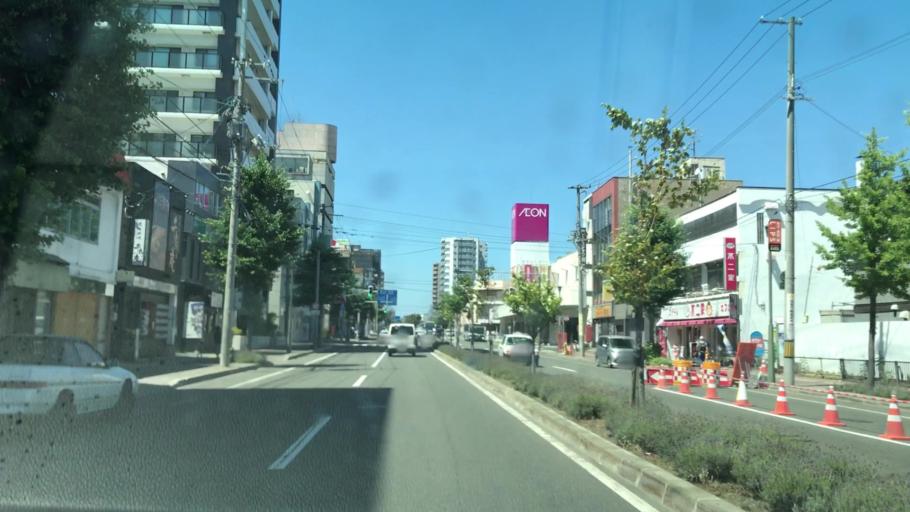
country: JP
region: Hokkaido
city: Sapporo
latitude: 43.0751
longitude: 141.3049
